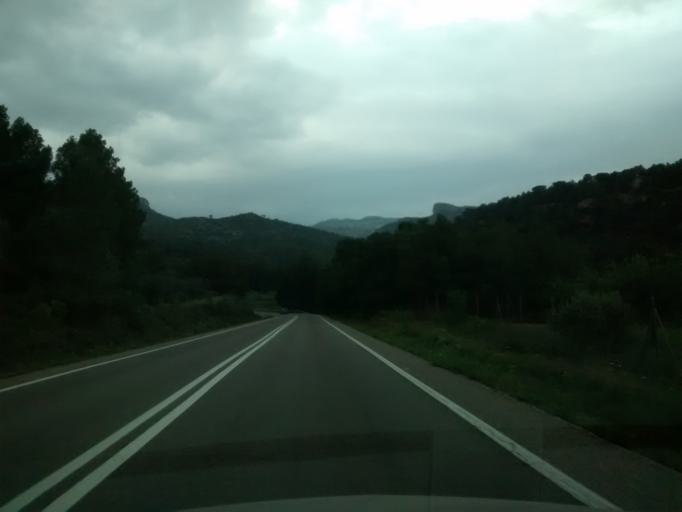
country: ES
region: Catalonia
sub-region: Provincia de Tarragona
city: Benifallet
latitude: 41.0203
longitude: 0.5008
